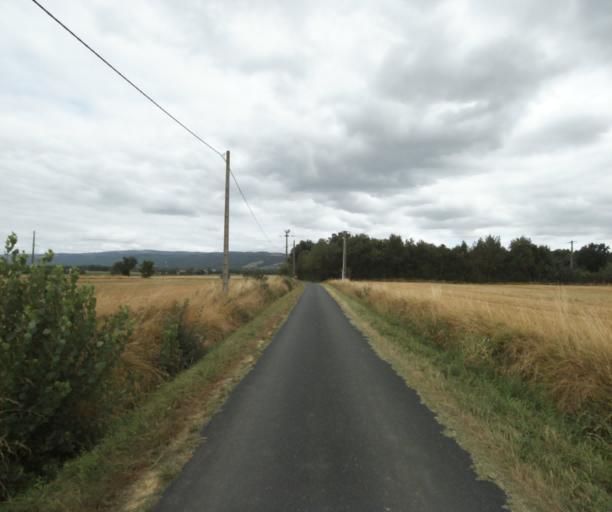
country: FR
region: Midi-Pyrenees
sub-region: Departement du Tarn
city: Soreze
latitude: 43.4713
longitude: 2.0395
